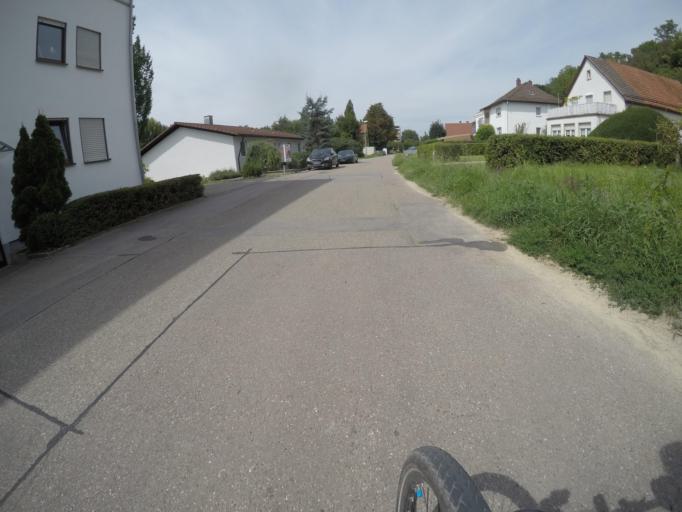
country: DE
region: Baden-Wuerttemberg
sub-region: Karlsruhe Region
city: Bruchsal
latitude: 49.1177
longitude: 8.6191
